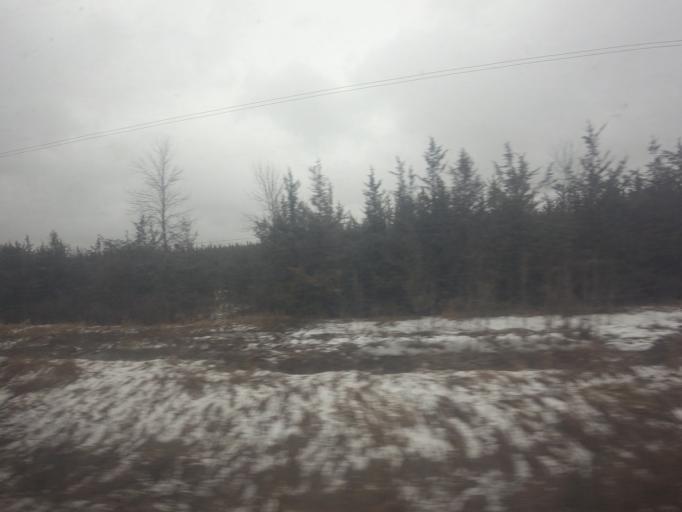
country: CA
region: Ontario
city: Deseronto
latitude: 44.2250
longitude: -77.0870
